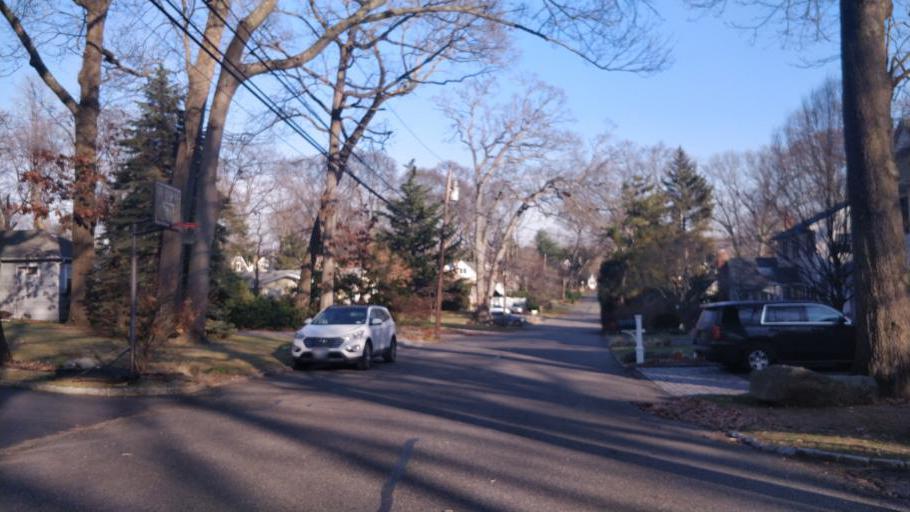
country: US
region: New York
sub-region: Nassau County
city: Bayville
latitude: 40.9051
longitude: -73.5772
